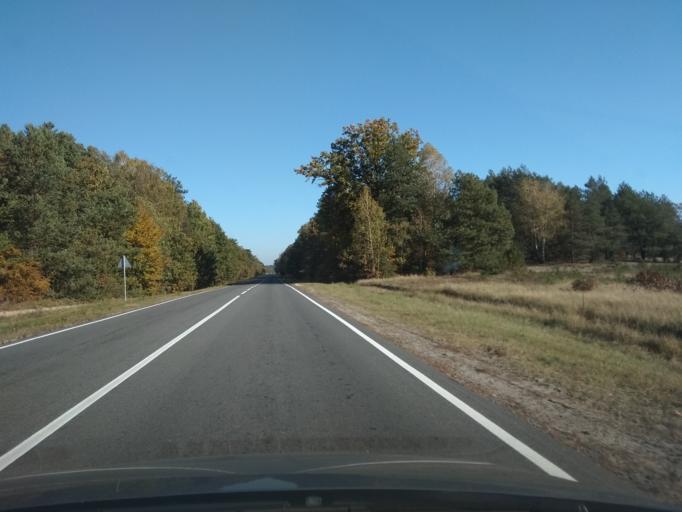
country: BY
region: Brest
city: Kobryn
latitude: 52.0148
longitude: 24.2344
